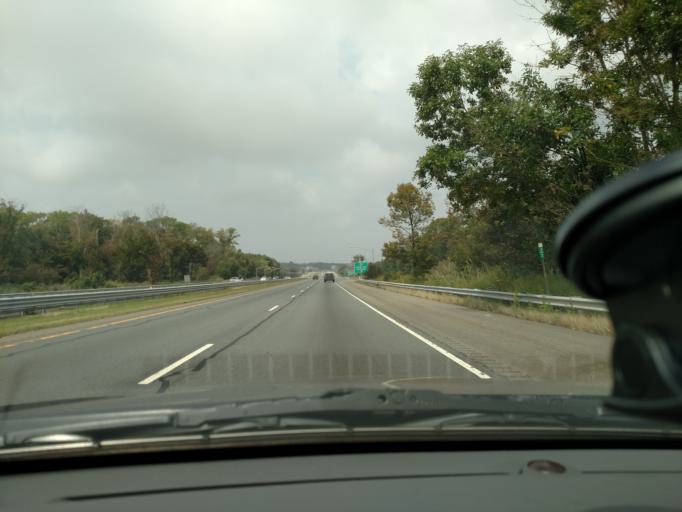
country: US
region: New Jersey
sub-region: Morris County
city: Madison
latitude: 40.7856
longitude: -74.4192
